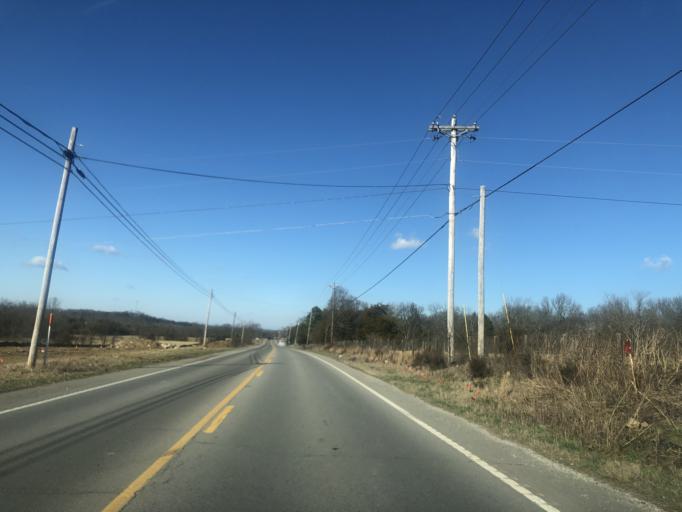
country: US
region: Tennessee
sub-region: Williamson County
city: Nolensville
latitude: 35.9318
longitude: -86.6589
